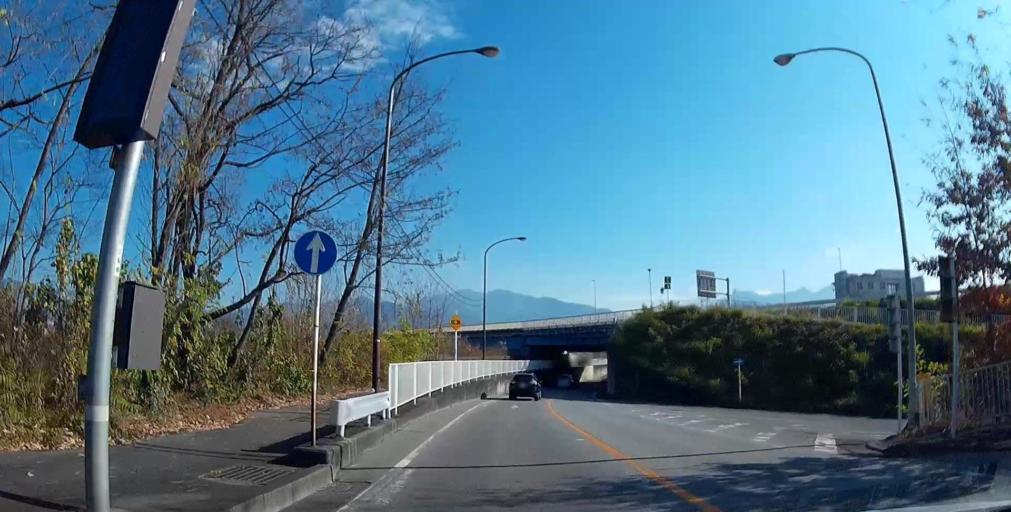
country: JP
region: Yamanashi
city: Isawa
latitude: 35.6467
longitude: 138.6673
